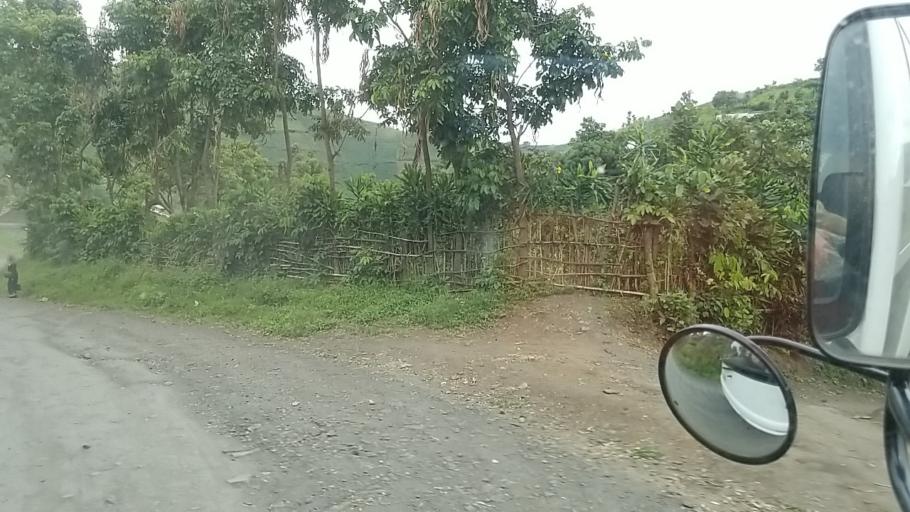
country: CD
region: Nord Kivu
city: Sake
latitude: -1.7600
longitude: 28.9872
